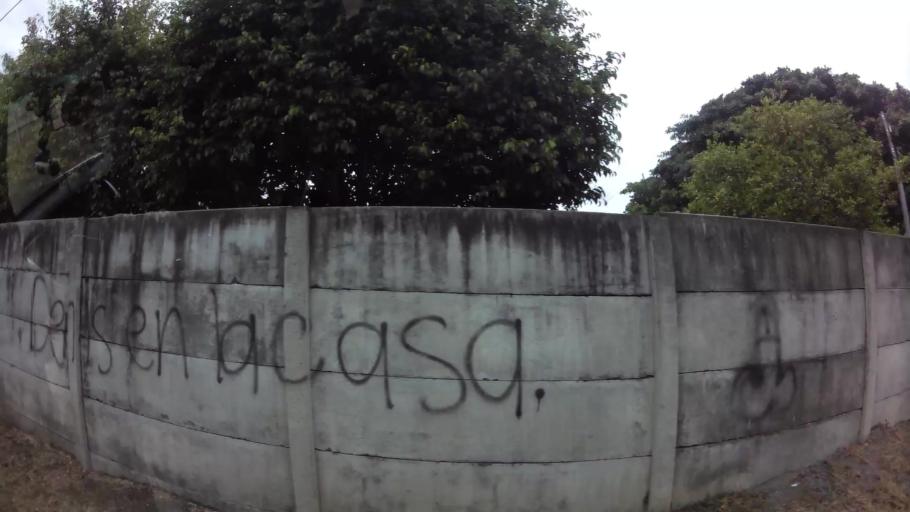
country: NI
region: Masaya
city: Ticuantepe
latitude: 12.0654
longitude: -86.1877
